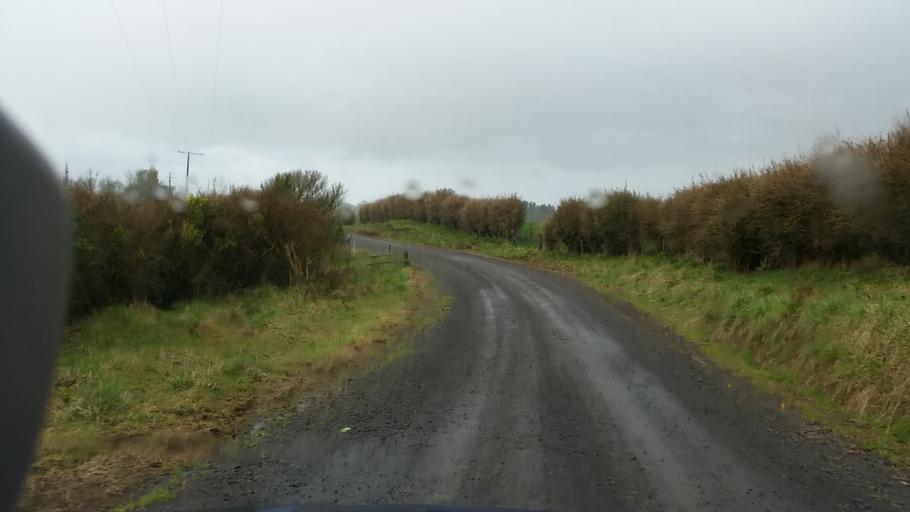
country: NZ
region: Taranaki
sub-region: South Taranaki District
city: Eltham
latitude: -39.2534
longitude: 174.2792
